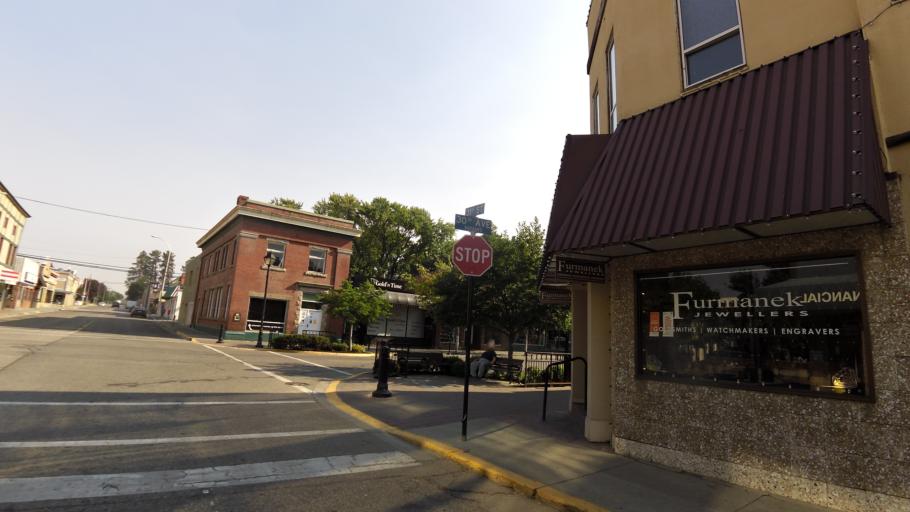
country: CA
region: British Columbia
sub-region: Regional District of North Okanagan
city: Vernon
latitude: 50.2635
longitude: -119.2723
